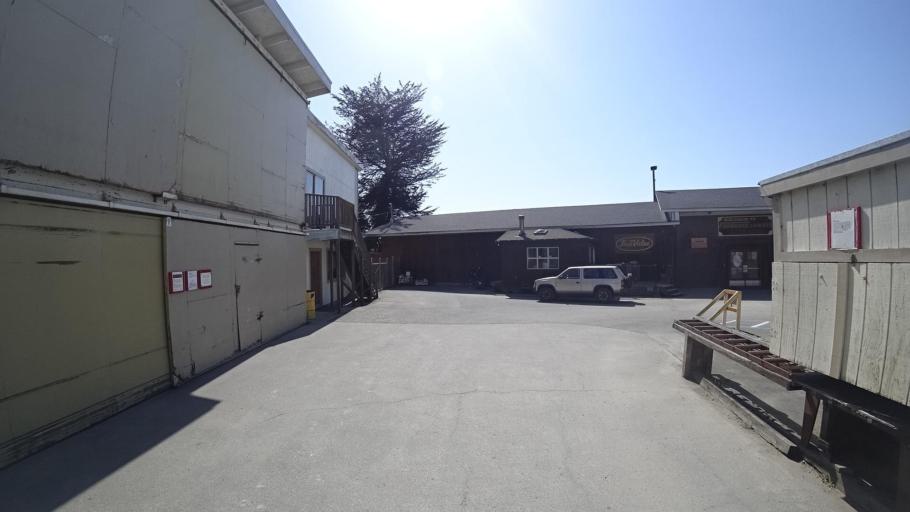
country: US
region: California
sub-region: Humboldt County
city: Fortuna
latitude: 40.5923
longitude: -124.1494
